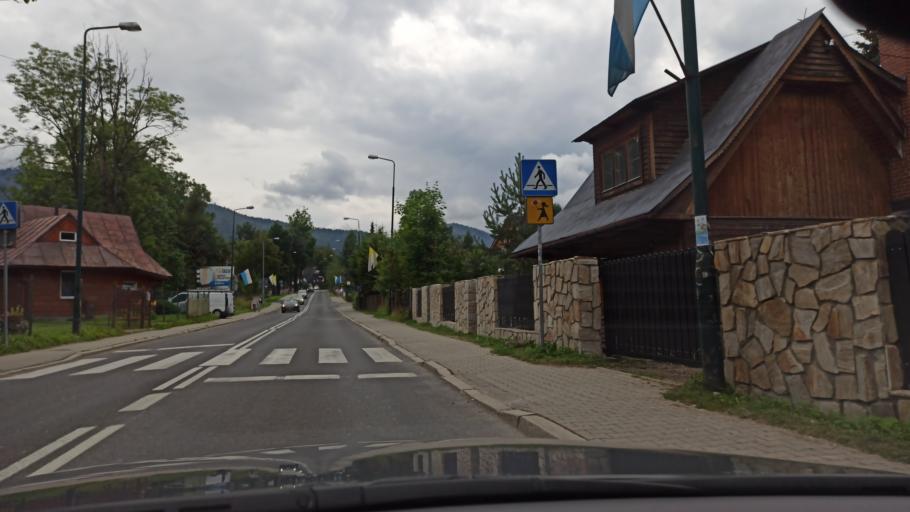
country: PL
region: Lesser Poland Voivodeship
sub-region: Powiat tatrzanski
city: Zakopane
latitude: 49.2885
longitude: 19.9318
